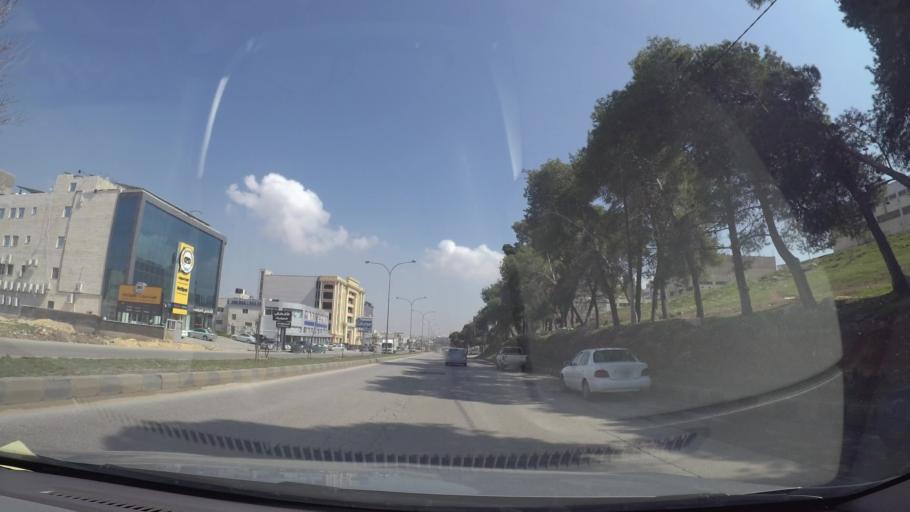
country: JO
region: Amman
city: Al Bunayyat ash Shamaliyah
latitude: 31.9116
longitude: 35.8971
